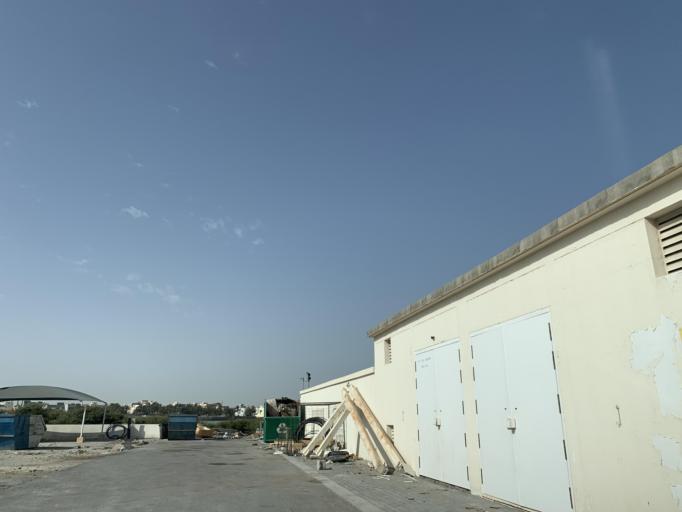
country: BH
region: Northern
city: Sitrah
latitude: 26.1527
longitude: 50.6112
